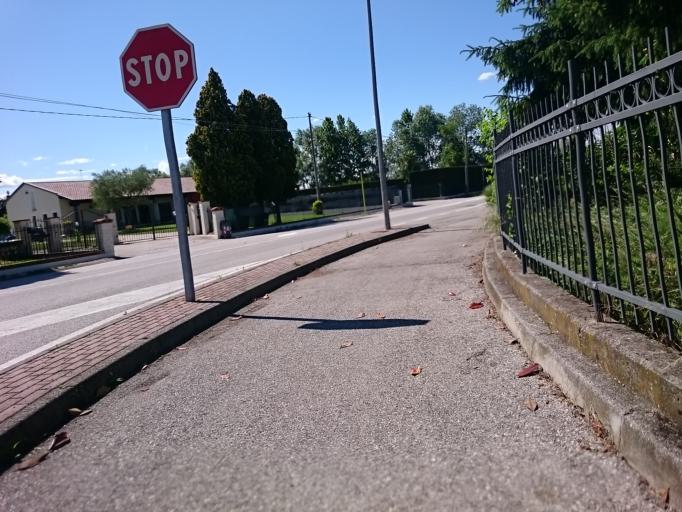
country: IT
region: Veneto
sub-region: Provincia di Venezia
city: Campolongo Maggiore
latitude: 45.3153
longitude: 12.0372
